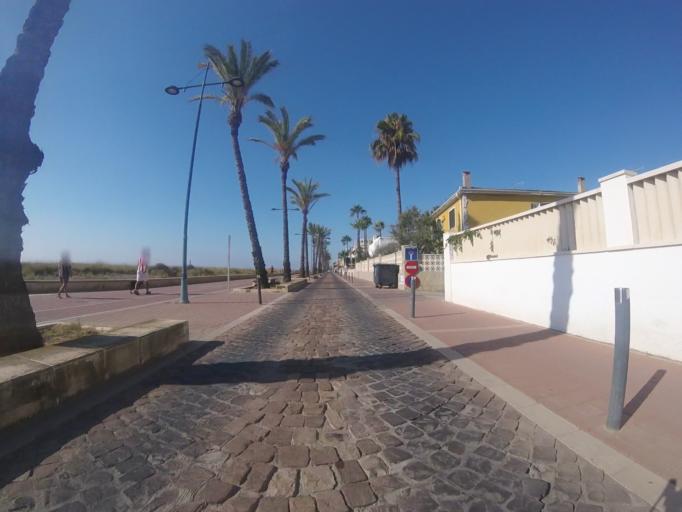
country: ES
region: Valencia
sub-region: Provincia de Castello
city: Benicarlo
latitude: 40.3993
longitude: 0.4166
